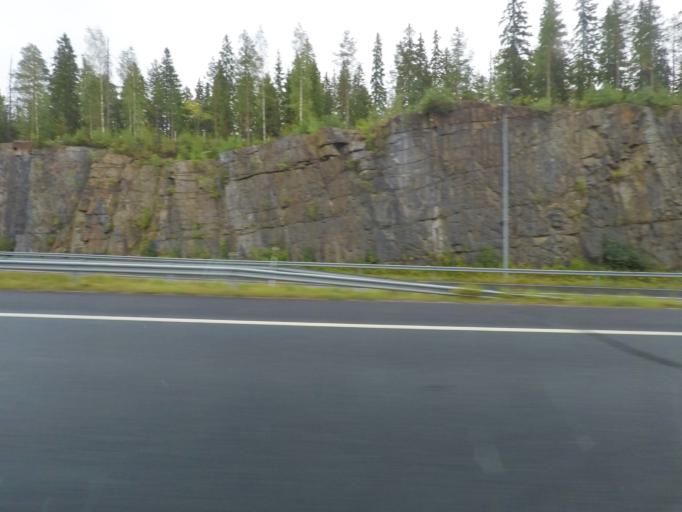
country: FI
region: Northern Savo
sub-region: Kuopio
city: Kuopio
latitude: 62.8176
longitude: 27.6115
